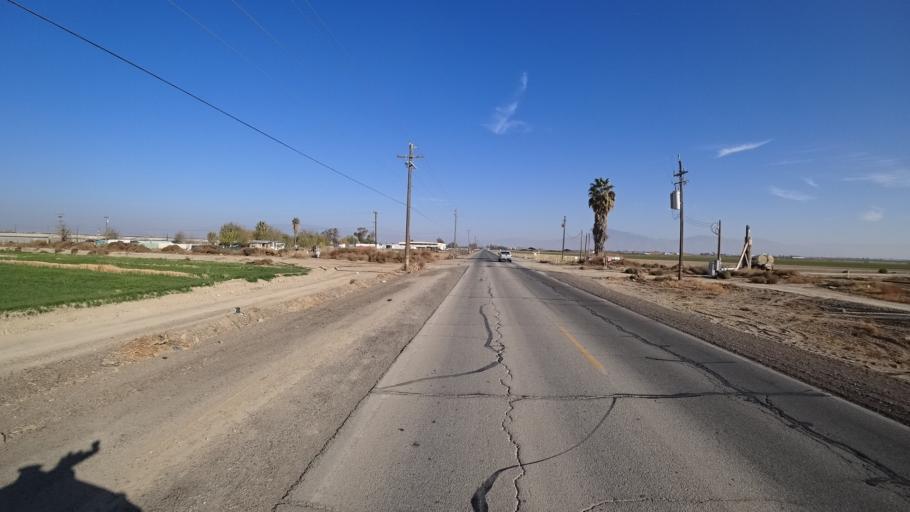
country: US
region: California
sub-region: Kern County
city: Lamont
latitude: 35.2960
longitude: -118.9504
